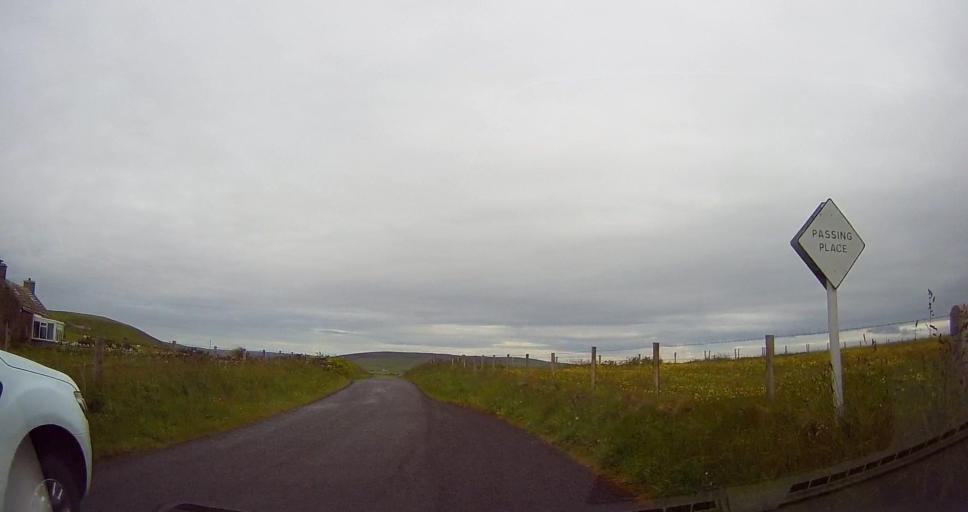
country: GB
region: Scotland
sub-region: Orkney Islands
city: Stromness
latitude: 59.1217
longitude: -3.2769
